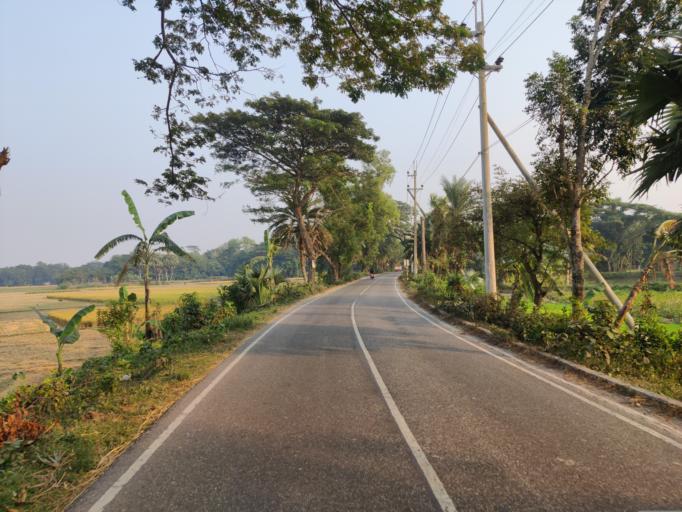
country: BD
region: Dhaka
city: Narsingdi
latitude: 24.0941
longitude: 90.7219
